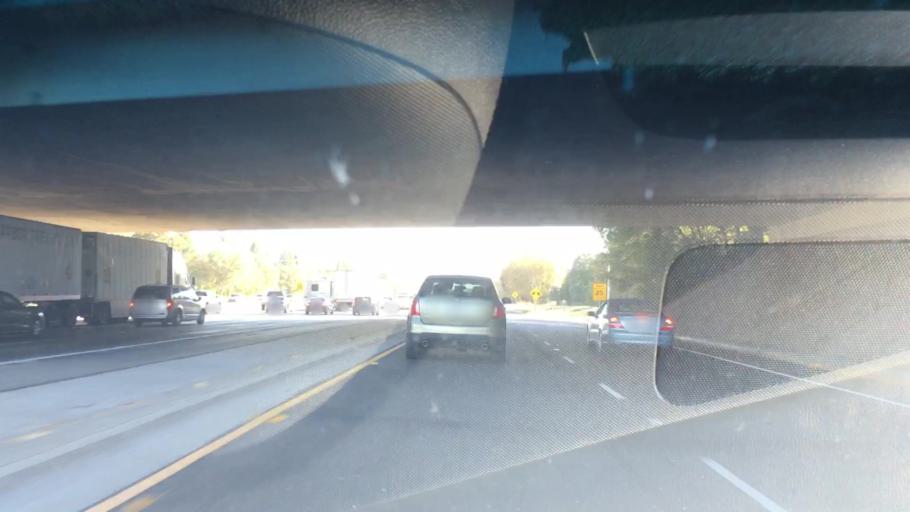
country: US
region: California
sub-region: Sacramento County
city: Parkway
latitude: 38.4957
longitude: -121.5170
